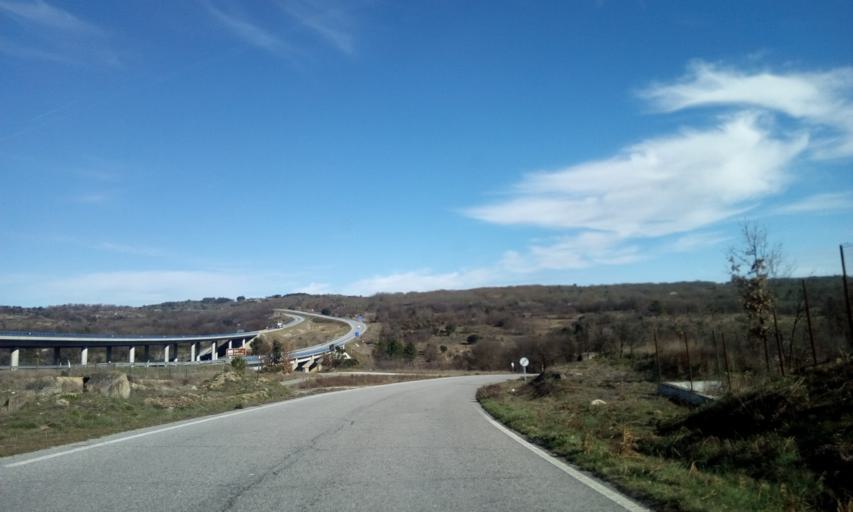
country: PT
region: Guarda
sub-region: Pinhel
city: Pinhel
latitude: 40.6043
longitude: -7.0352
